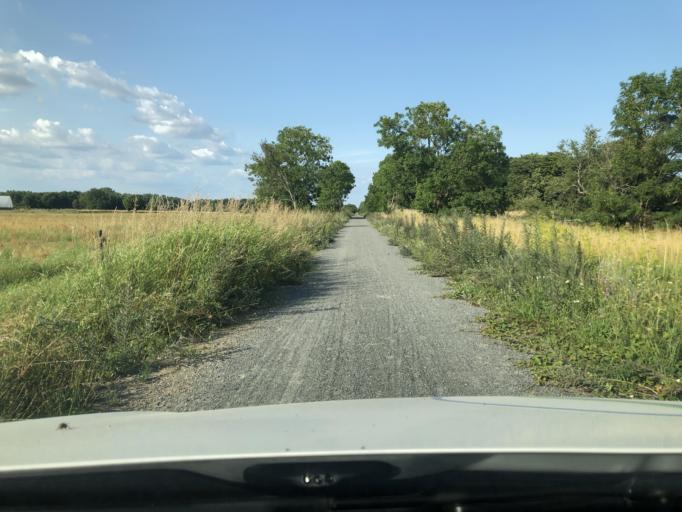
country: SE
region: Skane
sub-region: Kristianstads Kommun
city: Norra Asum
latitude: 55.9381
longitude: 14.1407
